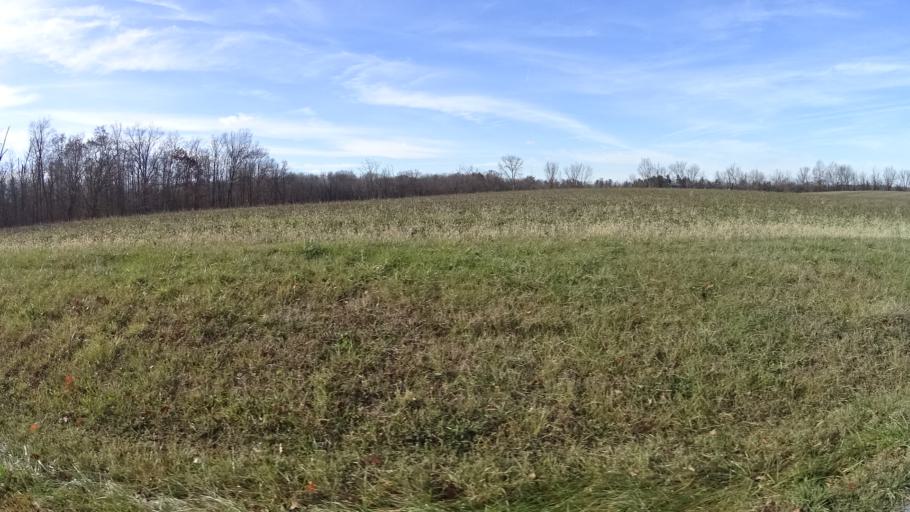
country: US
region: Ohio
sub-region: Lorain County
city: Wellington
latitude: 41.0651
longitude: -82.2396
